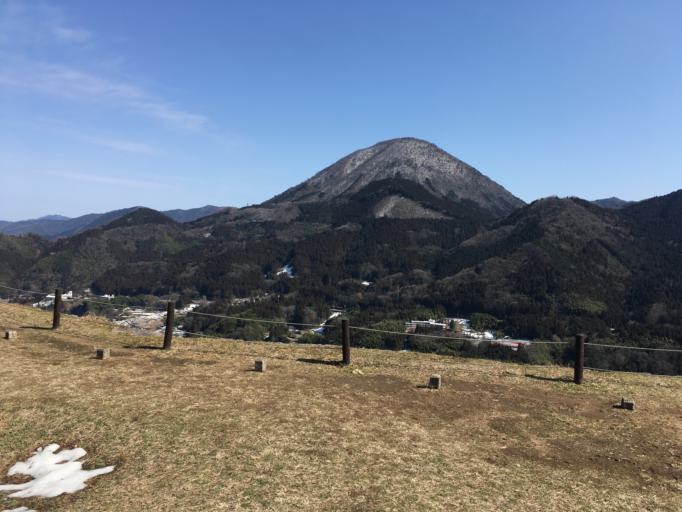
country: JP
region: Shimane
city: Masuda
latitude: 34.4599
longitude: 131.7641
